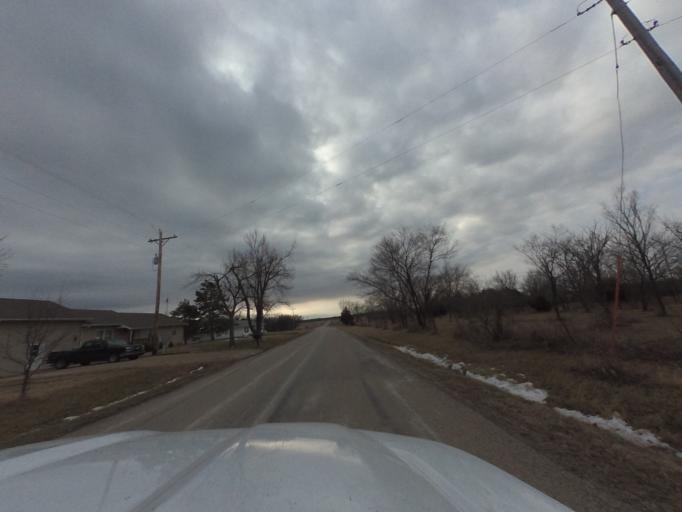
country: US
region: Kansas
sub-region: Chase County
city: Cottonwood Falls
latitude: 38.4217
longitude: -96.3734
